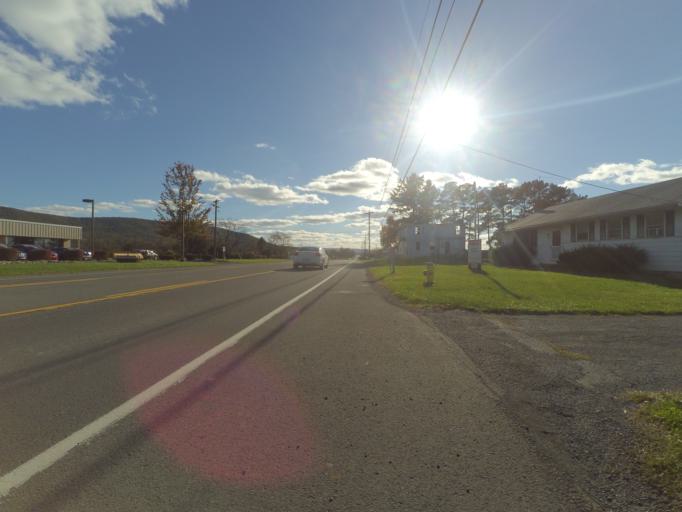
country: US
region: Pennsylvania
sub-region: Centre County
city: Houserville
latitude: 40.8440
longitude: -77.7951
